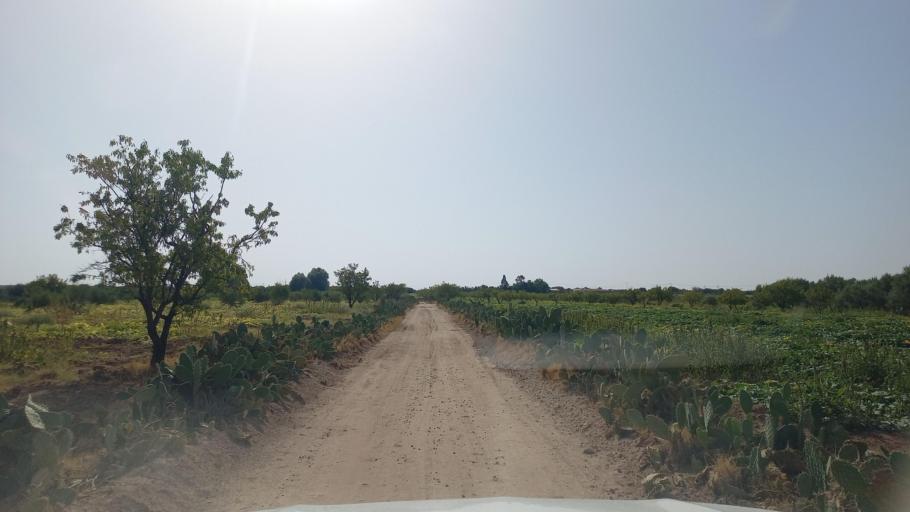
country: TN
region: Al Qasrayn
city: Kasserine
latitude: 35.2469
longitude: 9.0379
